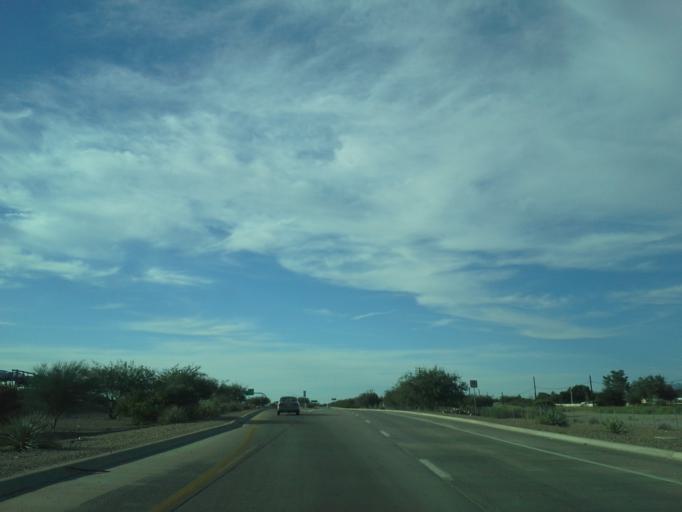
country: US
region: Arizona
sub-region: Pima County
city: Flowing Wells
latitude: 32.2949
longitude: -111.0297
